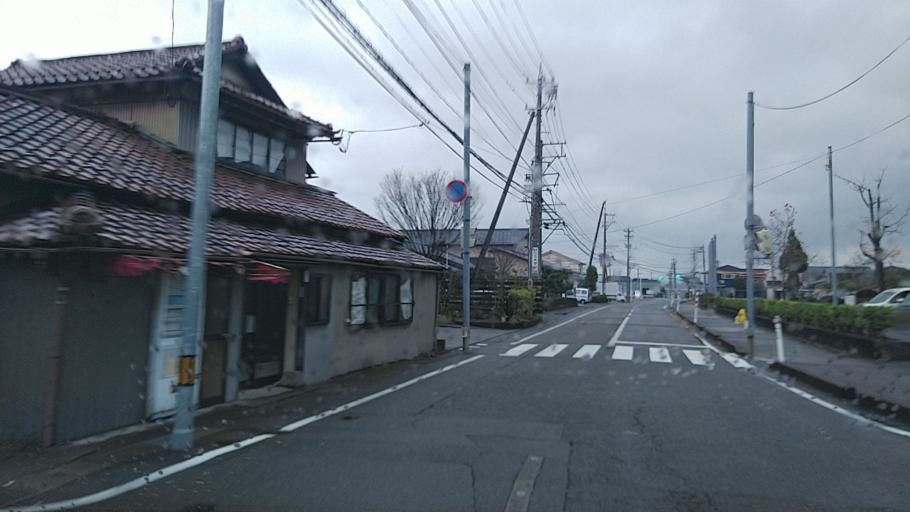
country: JP
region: Ishikawa
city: Komatsu
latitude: 36.3302
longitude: 136.3886
